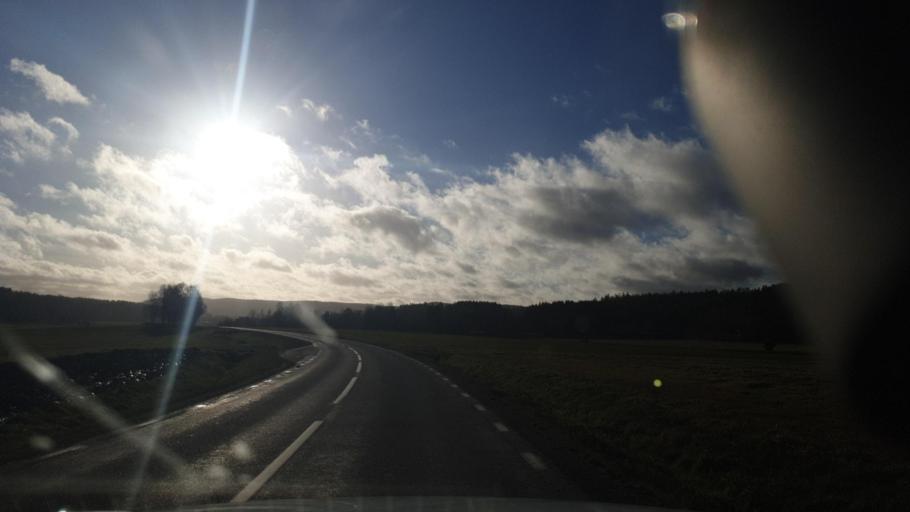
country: SE
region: Vaermland
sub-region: Eda Kommun
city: Amotfors
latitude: 59.6584
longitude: 12.1421
